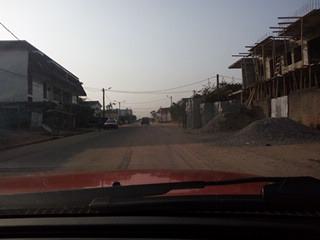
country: CI
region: Lagunes
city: Abobo
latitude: 5.3952
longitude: -3.9826
